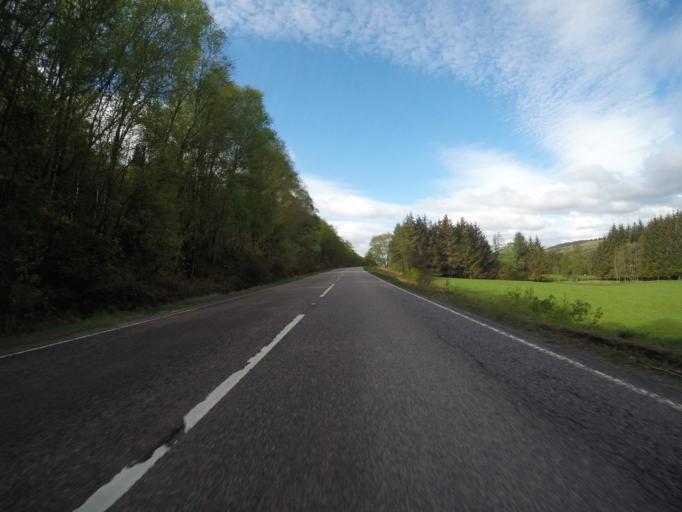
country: GB
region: Scotland
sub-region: Highland
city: Spean Bridge
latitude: 56.8700
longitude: -4.9965
